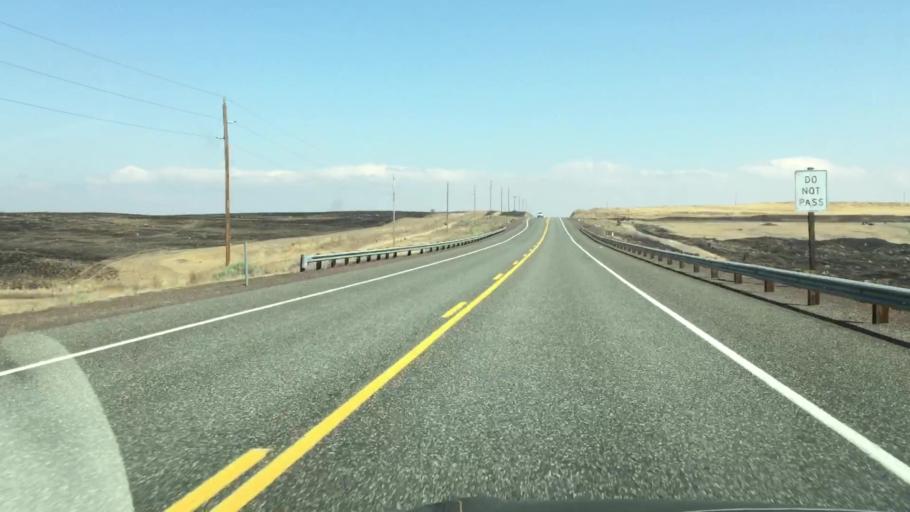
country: US
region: Oregon
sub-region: Wasco County
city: The Dalles
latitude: 45.3532
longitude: -121.1423
